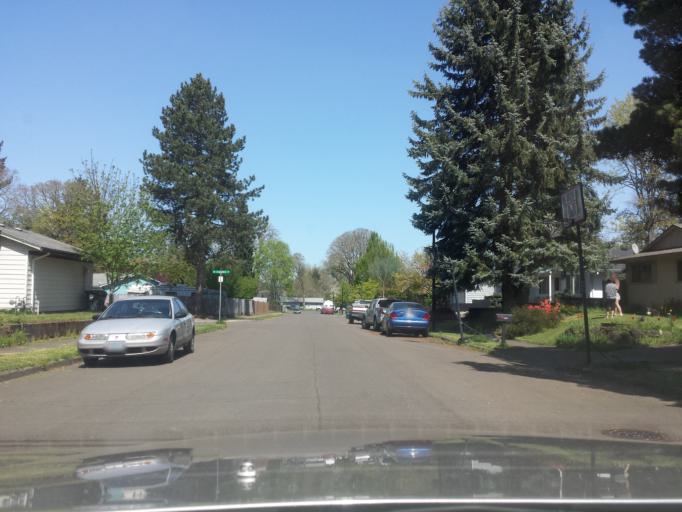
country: US
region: Oregon
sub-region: Washington County
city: Aloha
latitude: 45.4865
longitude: -122.8595
